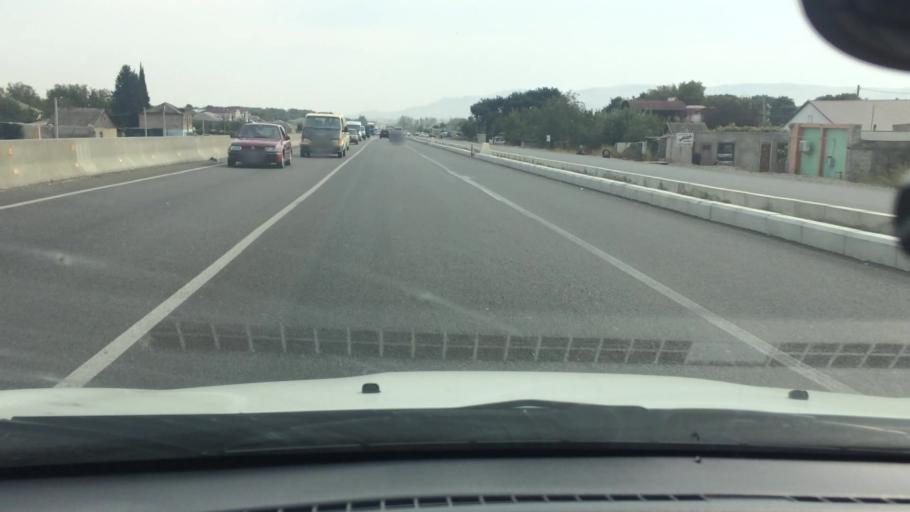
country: GE
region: T'bilisi
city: Tbilisi
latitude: 41.6359
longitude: 44.9175
